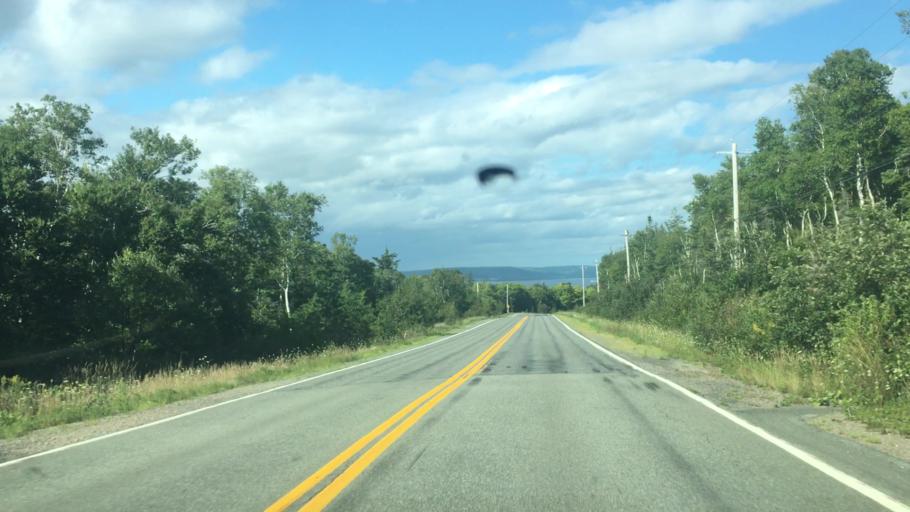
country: CA
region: Nova Scotia
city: Sydney
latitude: 45.8615
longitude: -60.6263
